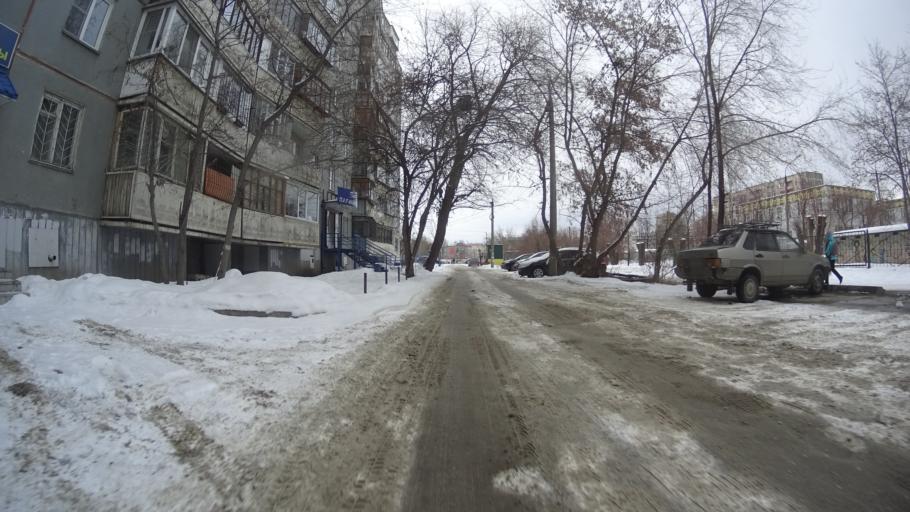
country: RU
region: Chelyabinsk
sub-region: Gorod Chelyabinsk
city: Chelyabinsk
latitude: 55.1767
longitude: 61.3411
